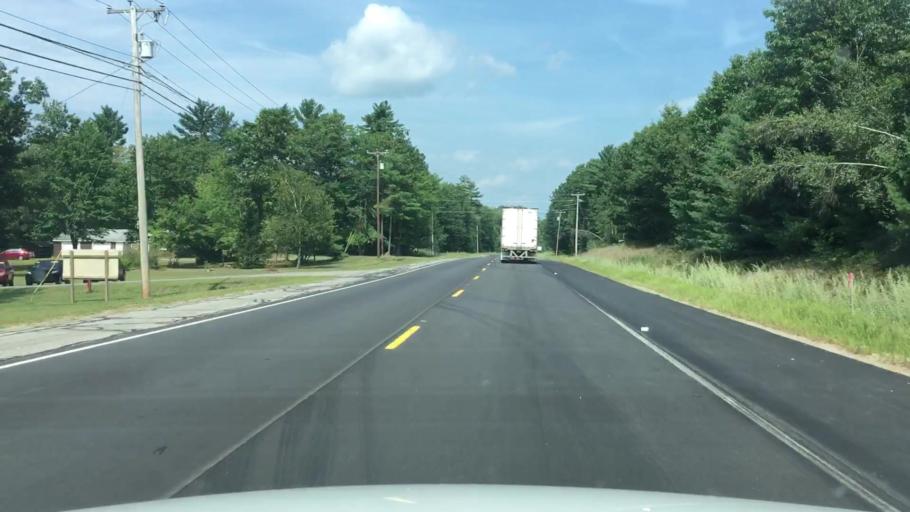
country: US
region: Maine
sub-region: Androscoggin County
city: Turner
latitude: 44.2754
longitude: -70.2707
